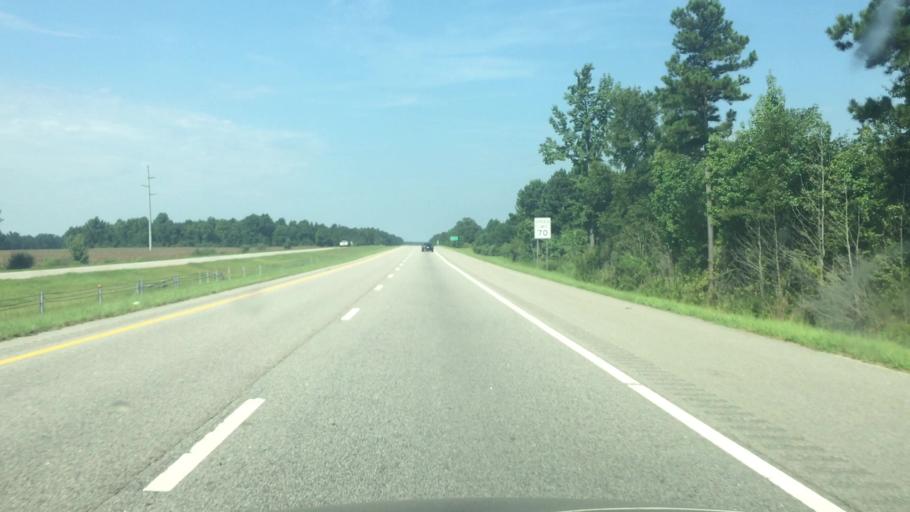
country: US
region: North Carolina
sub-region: Robeson County
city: Pembroke
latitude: 34.5990
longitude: -79.1459
